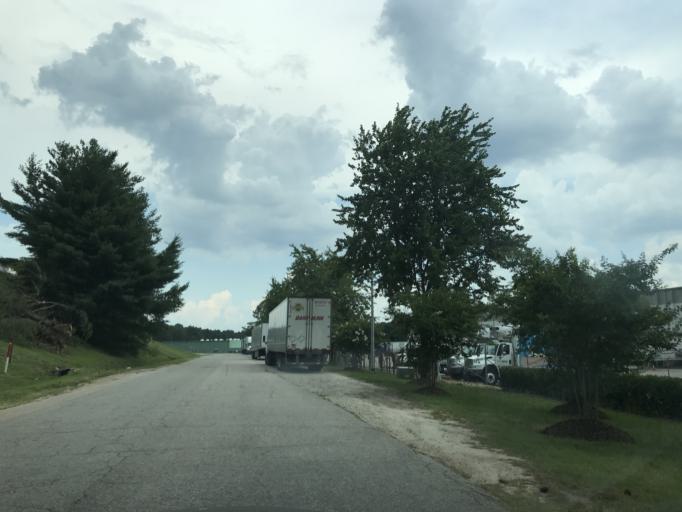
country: US
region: North Carolina
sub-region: Wake County
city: Wake Forest
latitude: 35.8855
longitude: -78.5782
